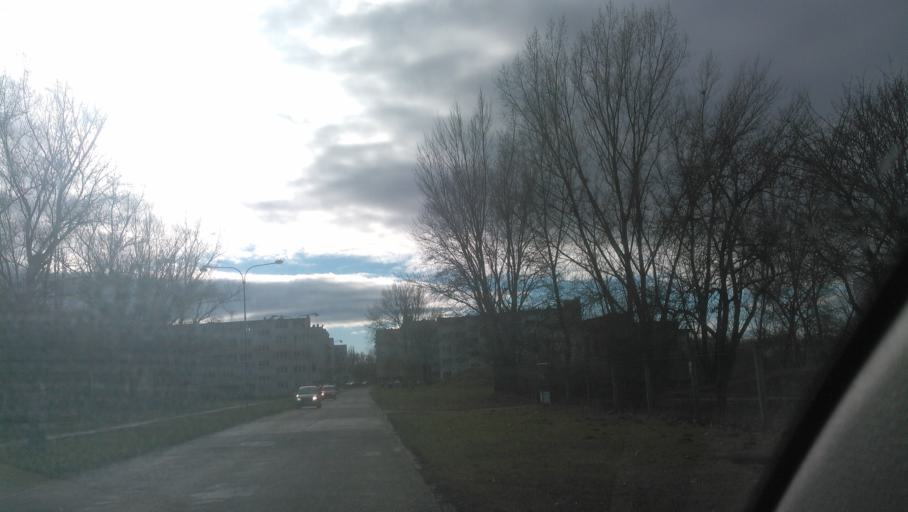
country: SK
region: Trnavsky
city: Hlohovec
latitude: 48.4219
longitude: 17.7841
